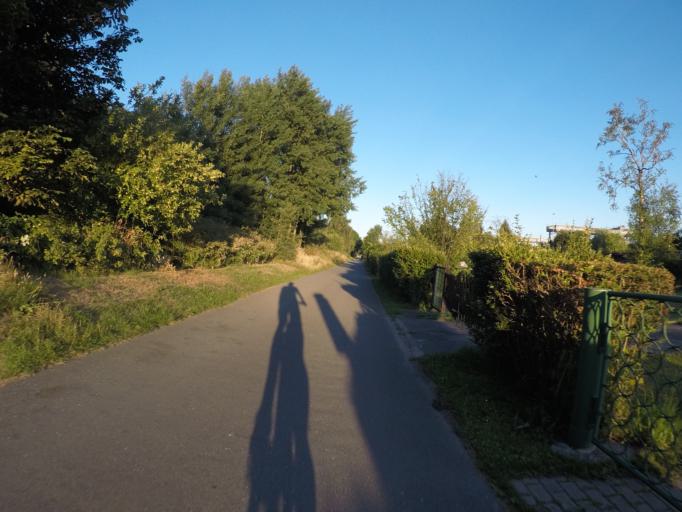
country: DE
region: Hamburg
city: Wandsbek
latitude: 53.5149
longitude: 10.1000
